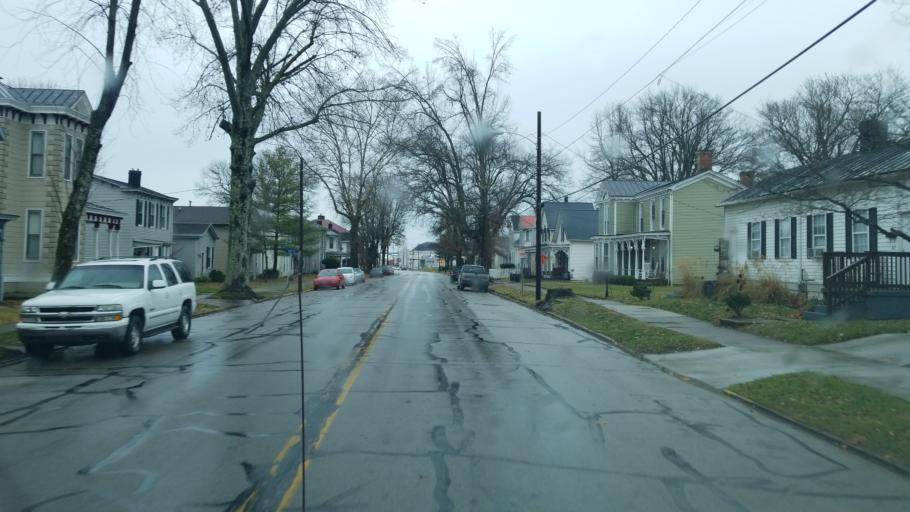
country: US
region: Kentucky
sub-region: Mason County
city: Maysville
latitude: 38.6429
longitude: -83.7552
